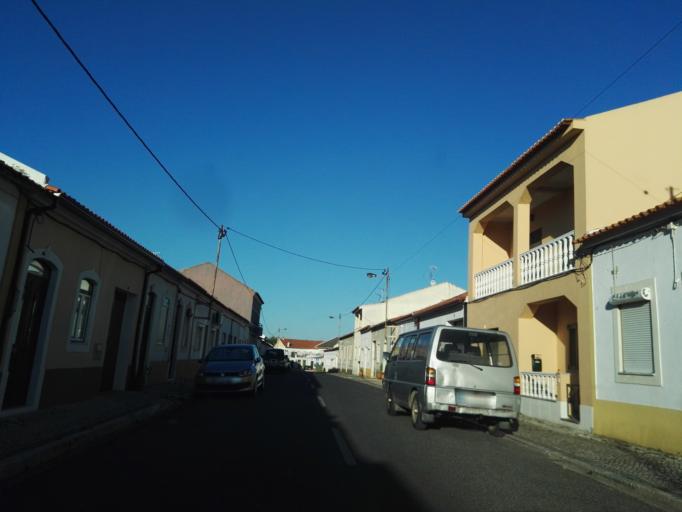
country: PT
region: Santarem
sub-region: Golega
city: Golega
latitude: 39.4045
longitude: -8.4877
